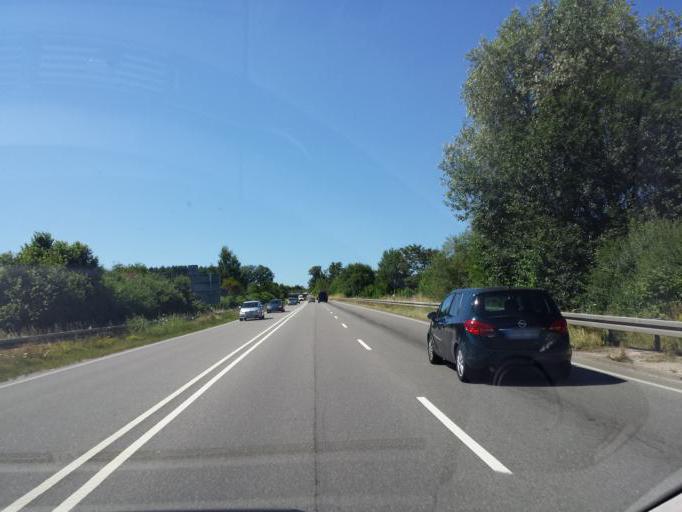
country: DE
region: Baden-Wuerttemberg
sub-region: Tuebingen Region
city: Owingen
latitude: 47.7959
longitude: 9.1411
